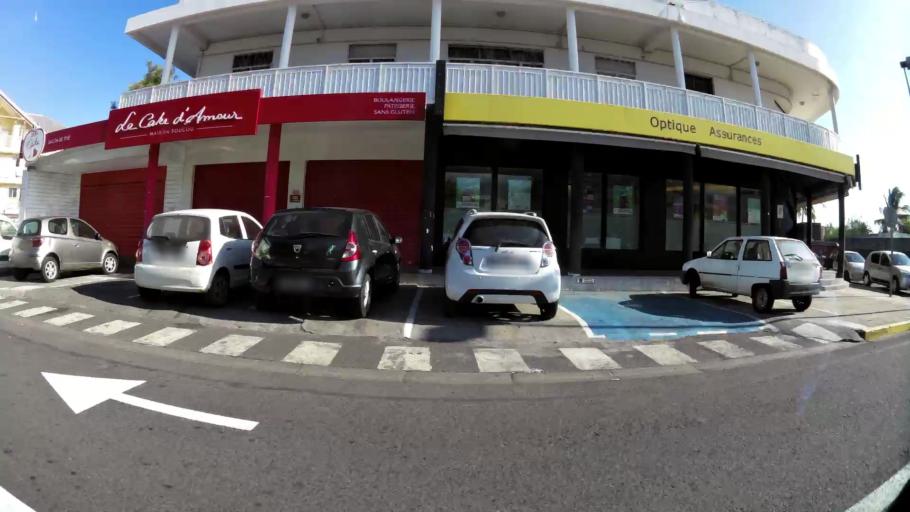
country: RE
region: Reunion
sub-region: Reunion
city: Saint-Louis
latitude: -21.2906
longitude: 55.4134
